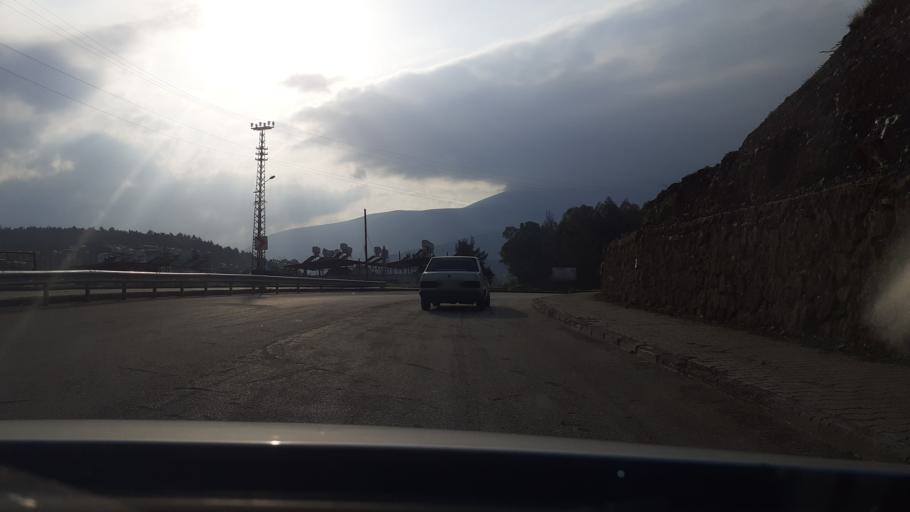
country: TR
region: Hatay
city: Kirikhan
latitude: 36.4979
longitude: 36.3448
